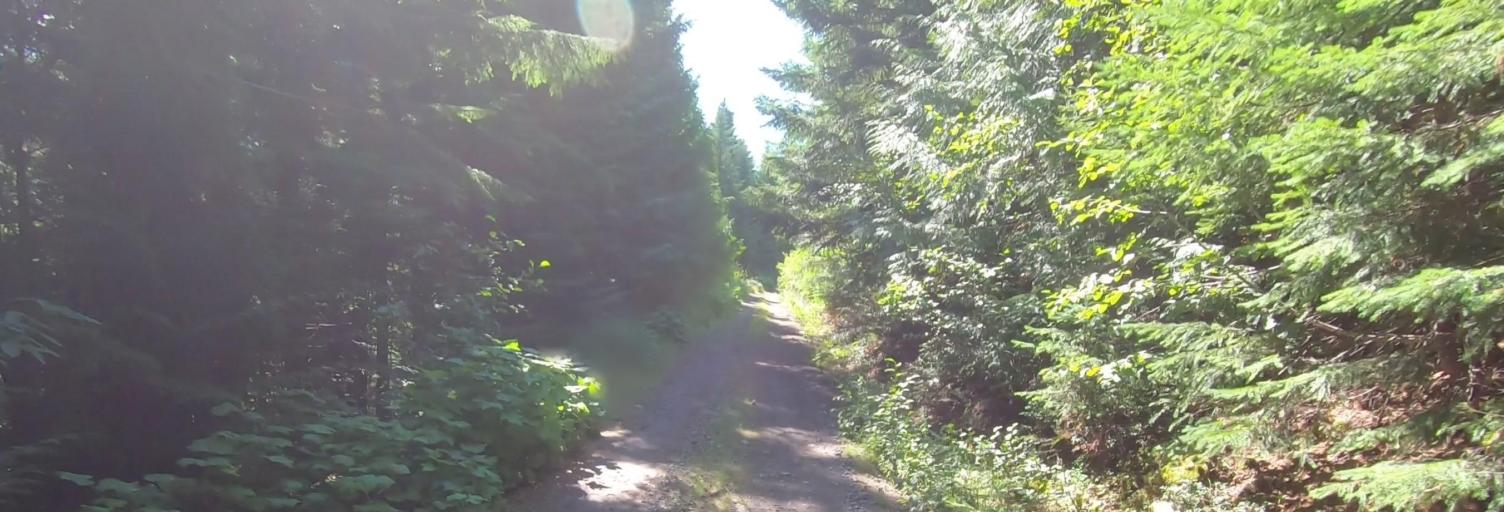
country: CA
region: British Columbia
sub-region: Fraser Valley Regional District
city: Chilliwack
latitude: 48.8623
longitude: -121.7791
